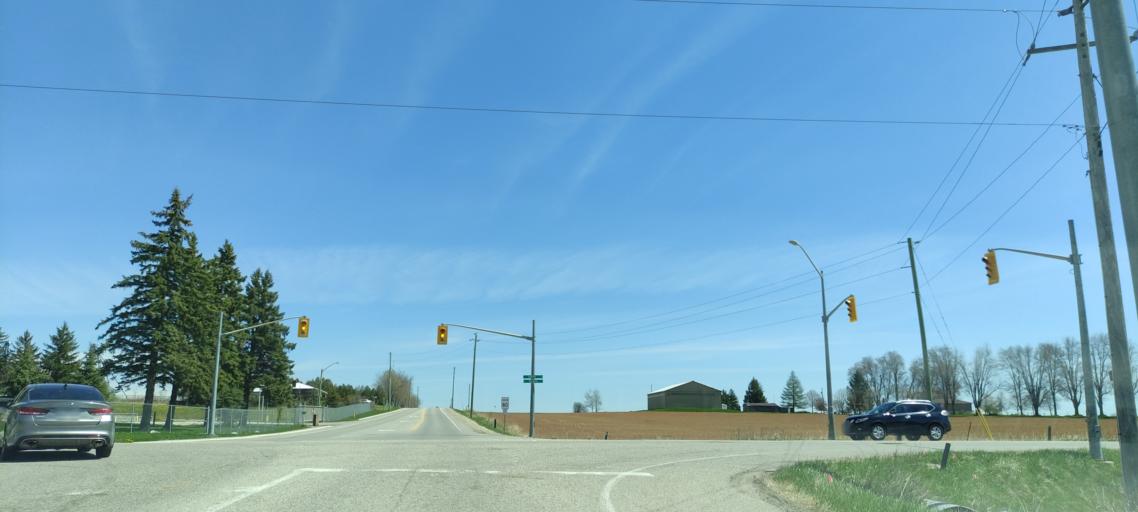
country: CA
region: Ontario
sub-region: Wellington County
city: Guelph
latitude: 43.6046
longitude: -80.3303
